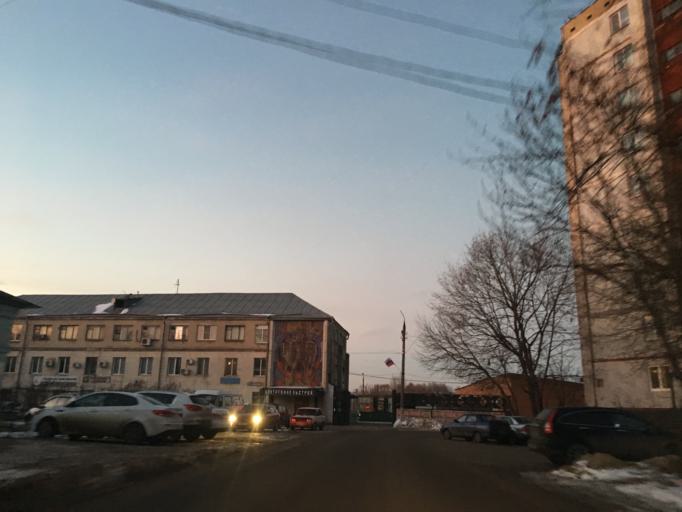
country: RU
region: Tula
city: Tula
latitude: 54.1834
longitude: 37.6320
